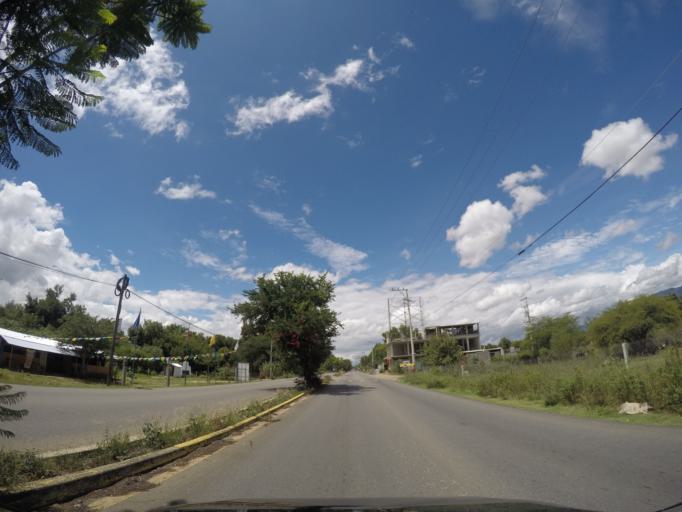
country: MX
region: Oaxaca
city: San Raymundo Jalpam
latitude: 16.9726
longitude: -96.7505
